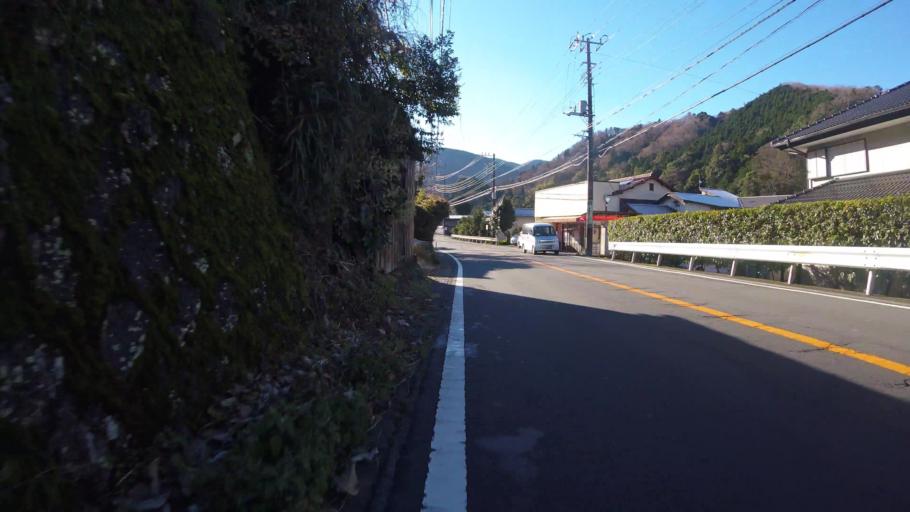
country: JP
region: Shizuoka
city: Heda
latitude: 34.8885
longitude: 138.9298
